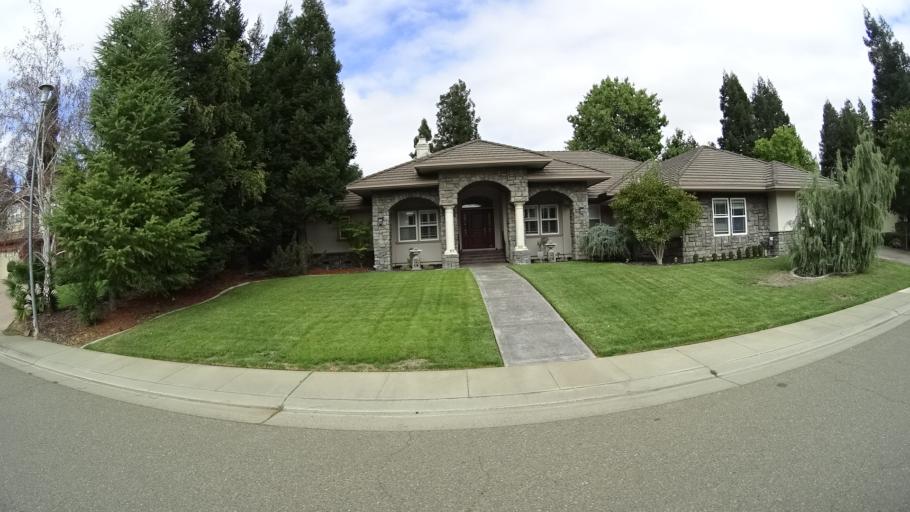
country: US
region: California
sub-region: Sacramento County
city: Laguna
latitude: 38.4166
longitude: -121.4387
